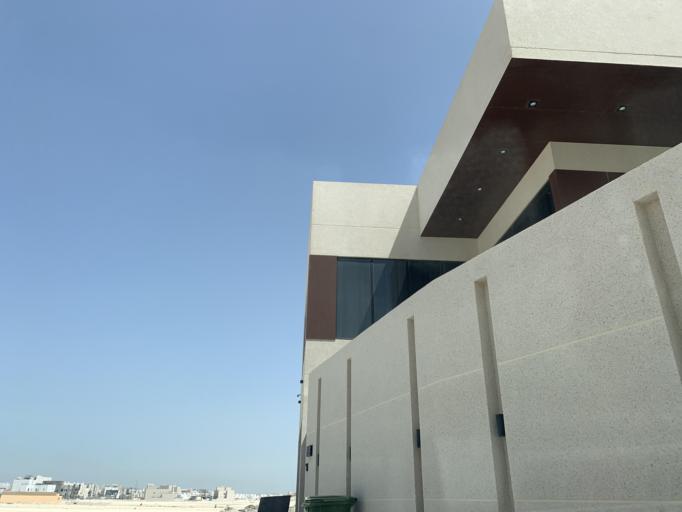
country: BH
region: Northern
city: Madinat `Isa
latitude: 26.1539
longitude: 50.5497
